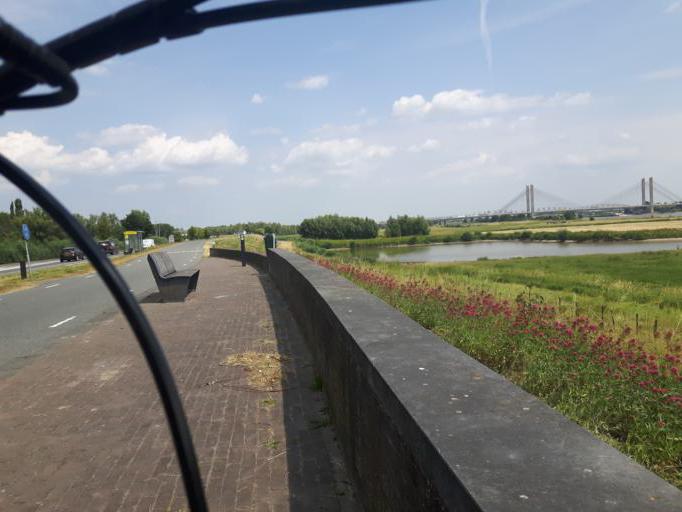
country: NL
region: Gelderland
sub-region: Gemeente Zaltbommel
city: Zaltbommel
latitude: 51.8211
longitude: 5.2402
